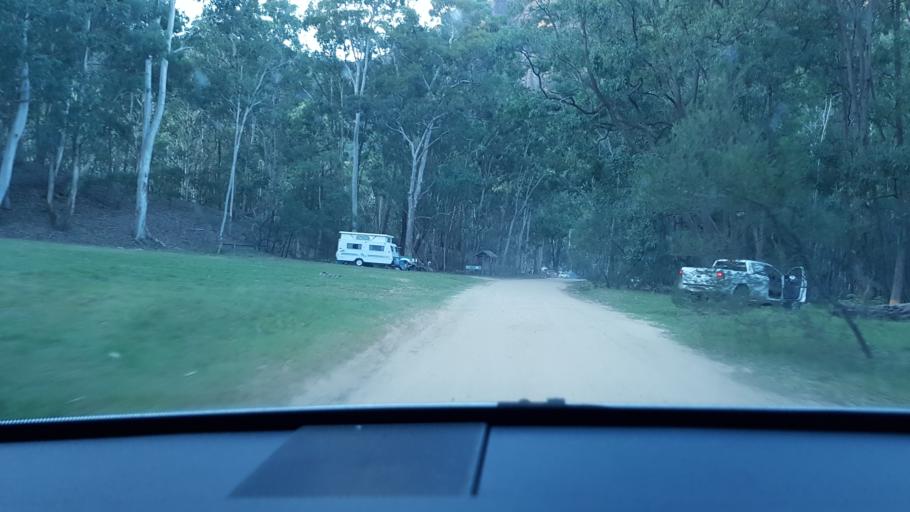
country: AU
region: New South Wales
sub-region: Lithgow
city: Portland
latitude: -33.1748
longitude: 150.2371
